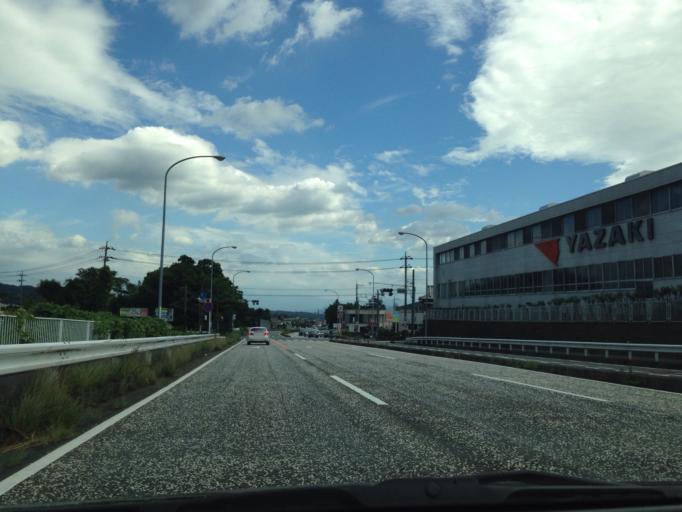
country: JP
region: Shizuoka
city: Gotemba
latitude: 35.2151
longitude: 138.9171
